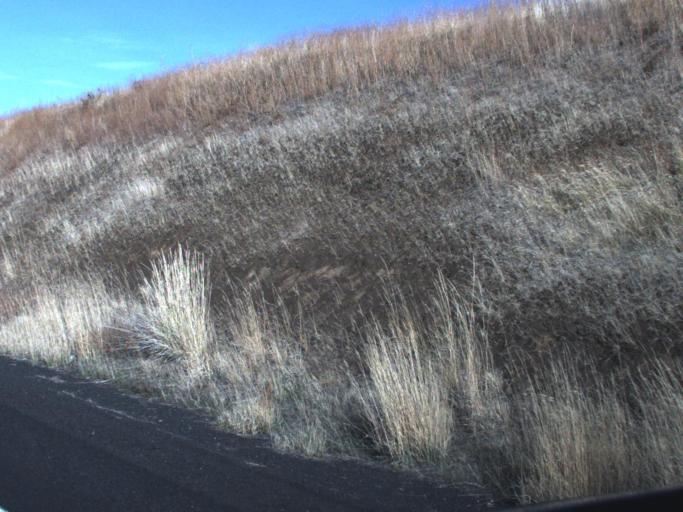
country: US
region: Washington
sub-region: Lincoln County
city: Davenport
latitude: 47.7826
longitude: -118.1736
